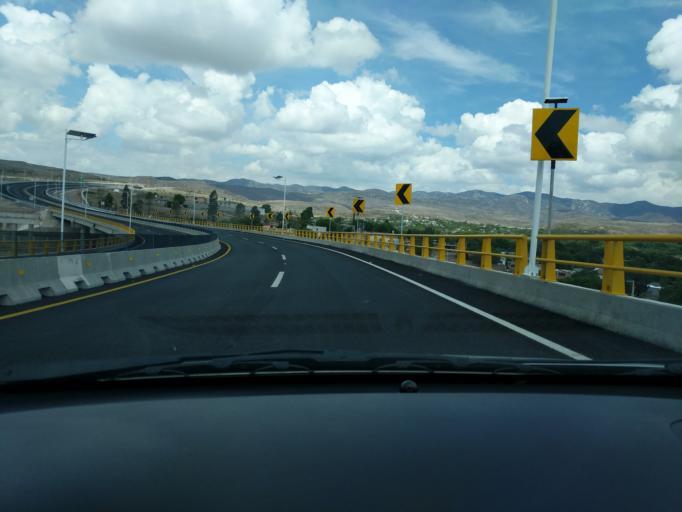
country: MX
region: San Luis Potosi
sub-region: Mexquitic de Carmona
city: Guadalupe Victoria
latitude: 22.1638
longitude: -101.0594
